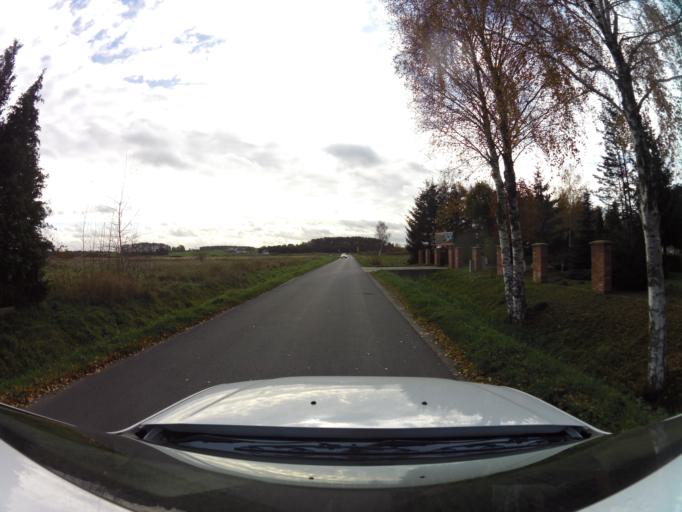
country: PL
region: West Pomeranian Voivodeship
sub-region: Powiat gryficki
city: Gryfice
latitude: 53.9154
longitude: 15.1785
